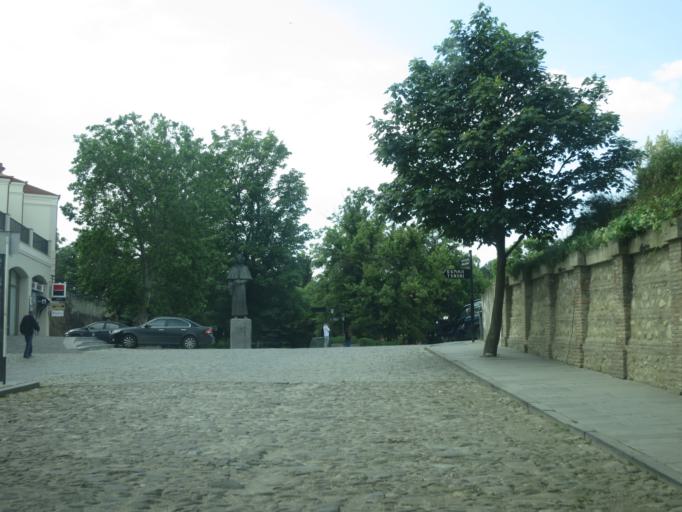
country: GE
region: Kakheti
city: Sighnaghi
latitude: 41.6206
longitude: 45.9225
